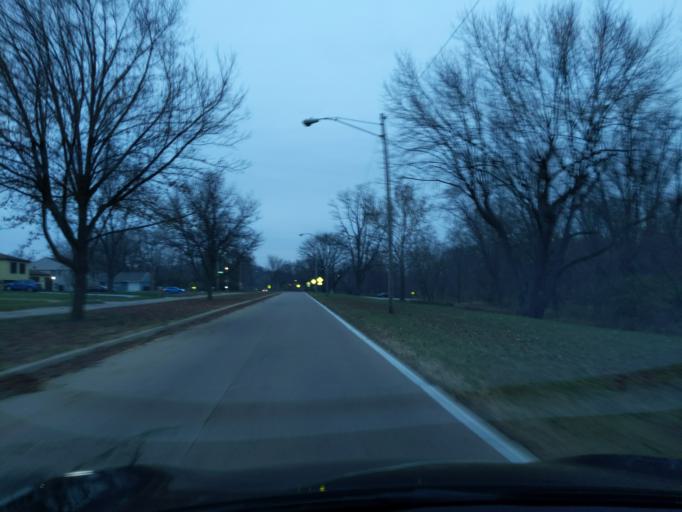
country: US
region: Indiana
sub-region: Saint Joseph County
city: Georgetown
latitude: 41.7268
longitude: -86.2694
